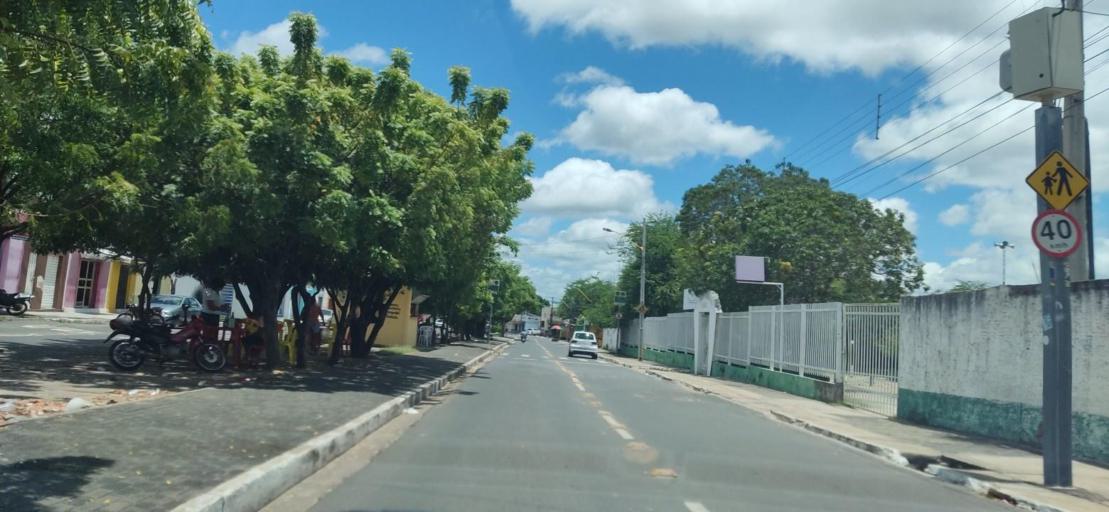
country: BR
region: Piaui
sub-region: Teresina
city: Teresina
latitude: -5.1498
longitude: -42.7840
